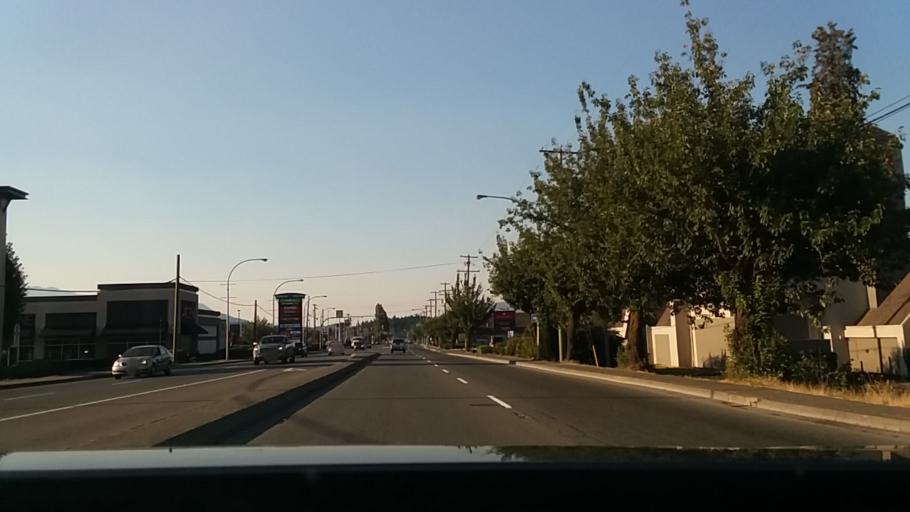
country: CA
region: British Columbia
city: Duncan
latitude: 48.7737
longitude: -123.6988
